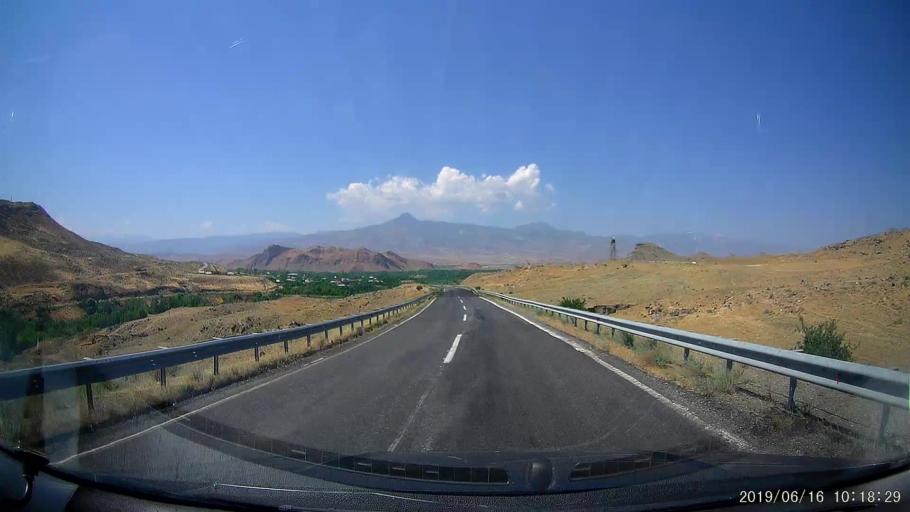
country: TR
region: Igdir
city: Tuzluca
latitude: 40.1600
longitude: 43.6675
